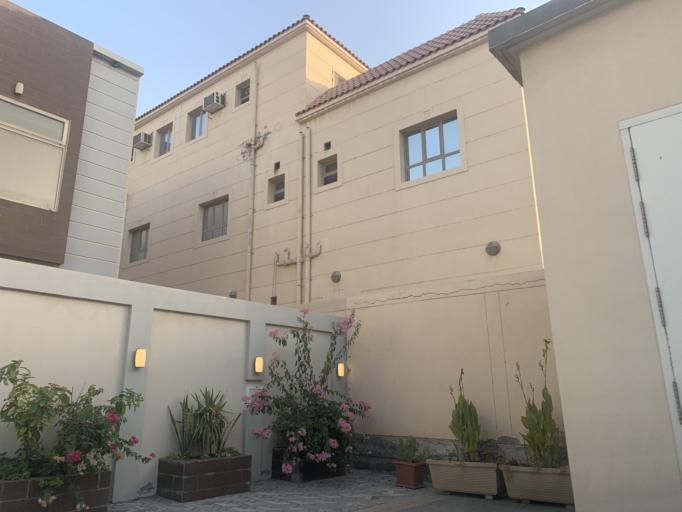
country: BH
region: Manama
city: Jidd Hafs
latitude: 26.1997
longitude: 50.5300
